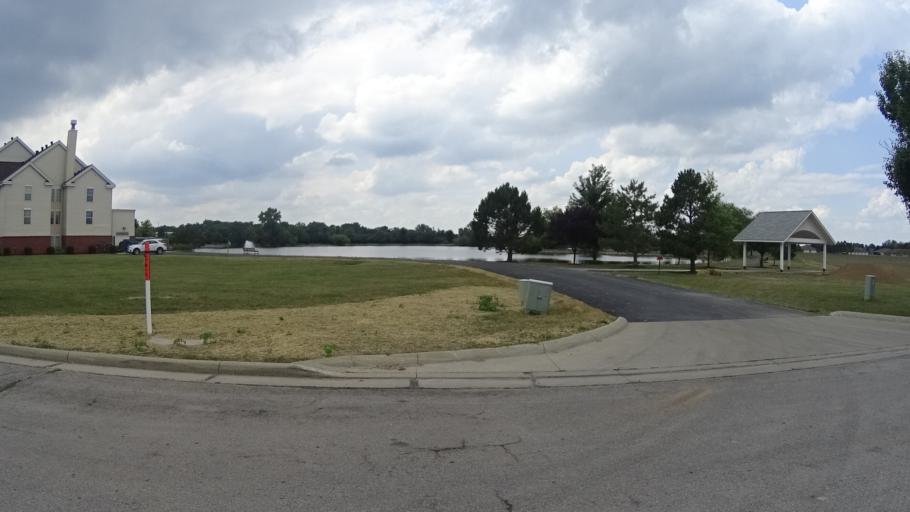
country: US
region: Ohio
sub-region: Erie County
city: Sandusky
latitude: 41.4456
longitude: -82.7761
